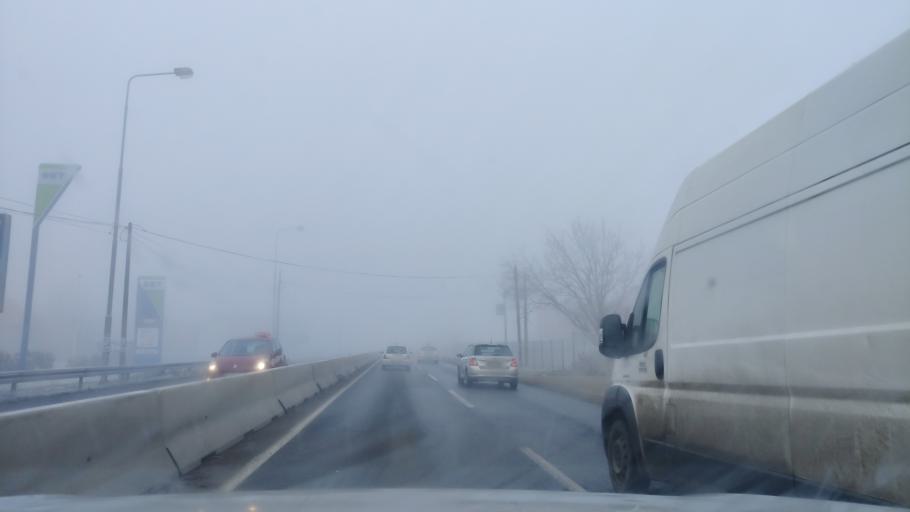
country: RS
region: Central Serbia
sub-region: Belgrade
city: Stari Grad
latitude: 44.8628
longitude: 20.4774
